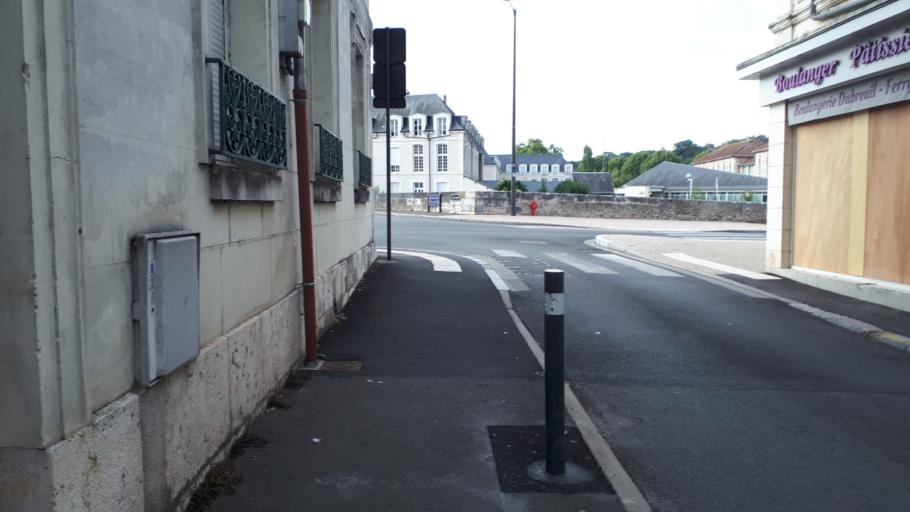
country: FR
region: Centre
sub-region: Departement du Loir-et-Cher
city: Vendome
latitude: 47.7953
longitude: 1.0638
